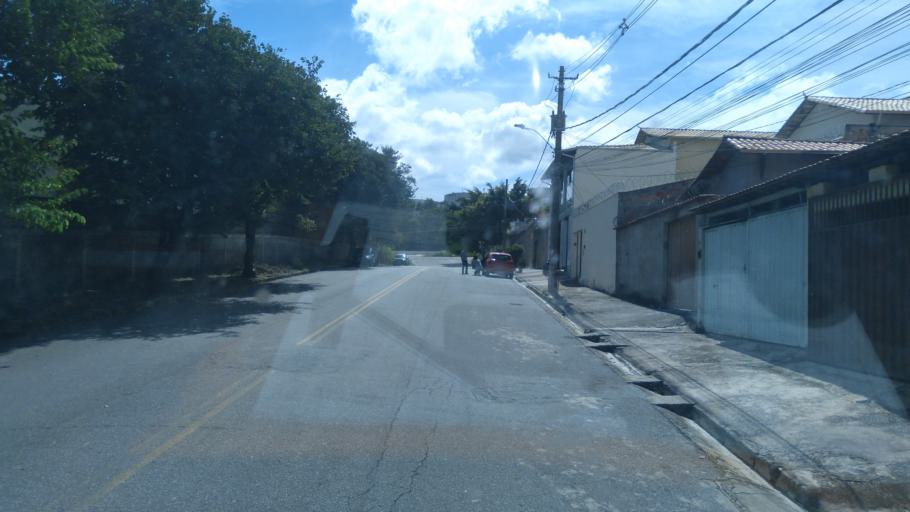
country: BR
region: Minas Gerais
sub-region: Belo Horizonte
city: Belo Horizonte
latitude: -19.8587
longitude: -43.8945
